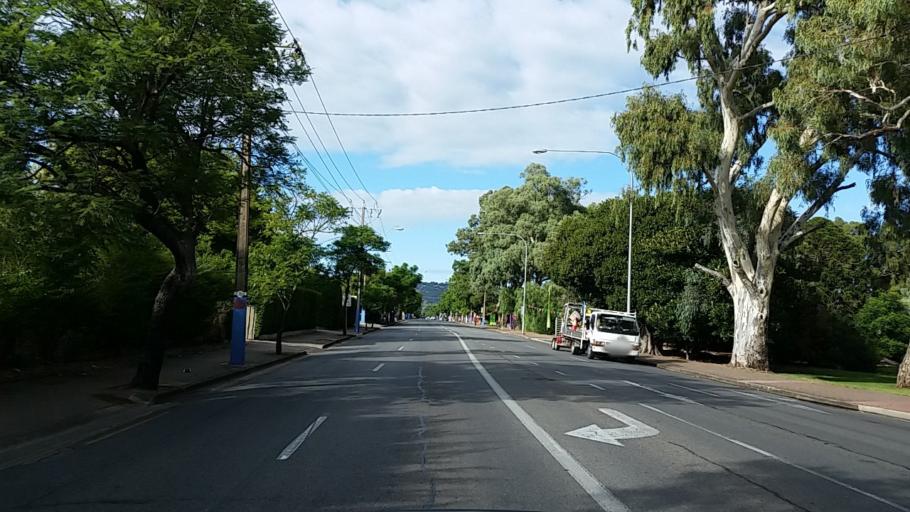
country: AU
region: South Australia
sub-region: Unley
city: Fullarton
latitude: -34.9571
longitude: 138.6259
